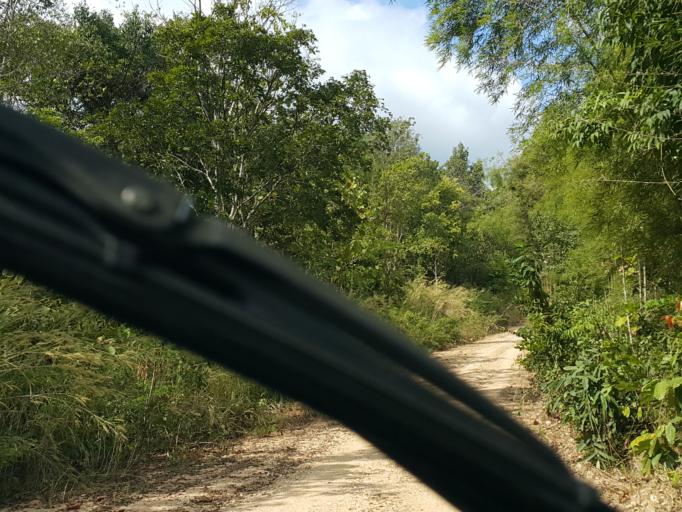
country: TH
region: Lampang
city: Chae Hom
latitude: 18.5641
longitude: 99.4455
